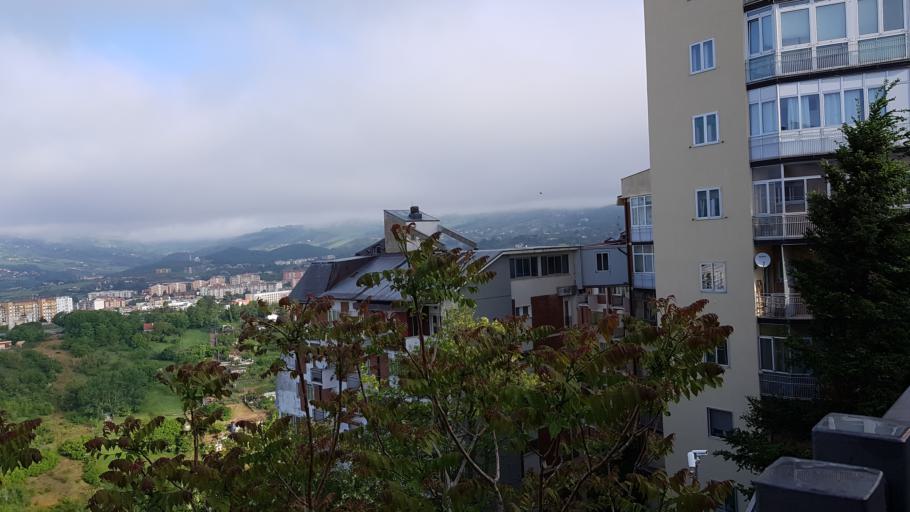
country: IT
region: Basilicate
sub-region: Provincia di Potenza
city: Potenza
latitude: 40.6368
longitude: 15.7990
